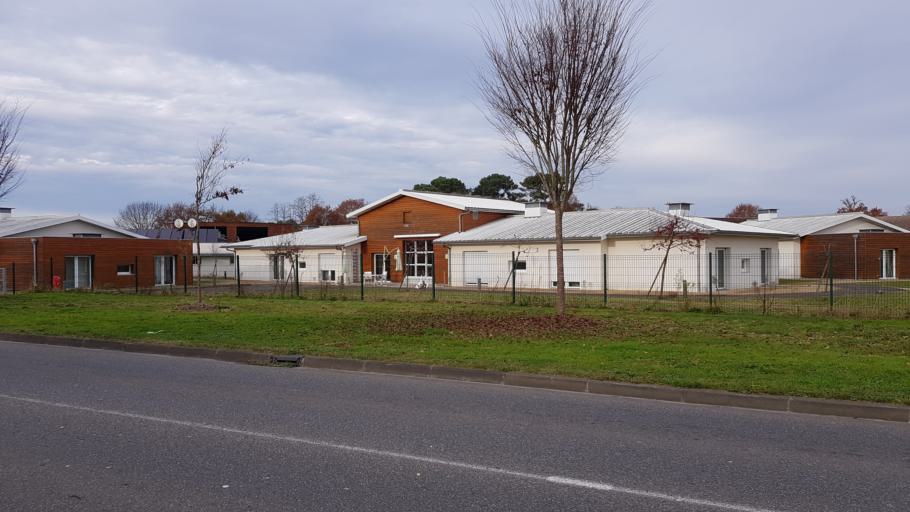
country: FR
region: Aquitaine
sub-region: Departement des Landes
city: Saint-Paul-les-Dax
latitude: 43.7359
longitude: -1.0494
